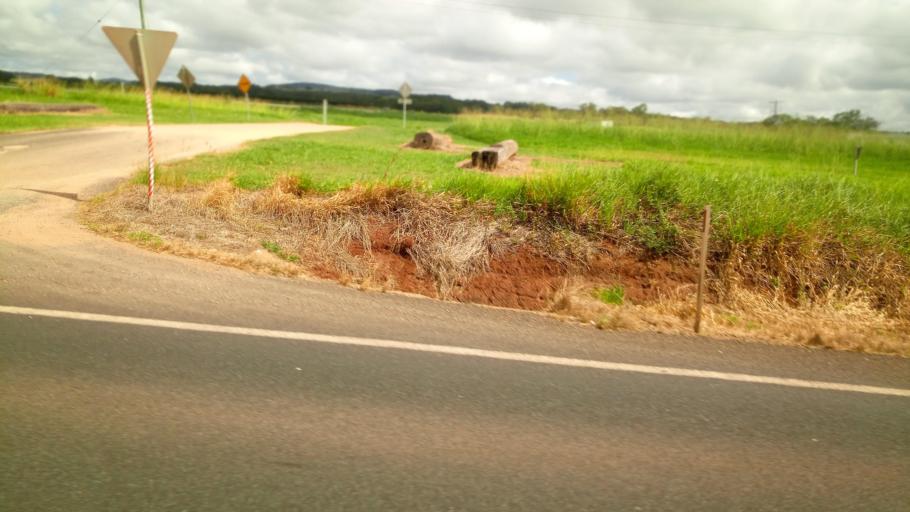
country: AU
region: Queensland
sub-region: Tablelands
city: Tolga
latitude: -17.2116
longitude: 145.4787
